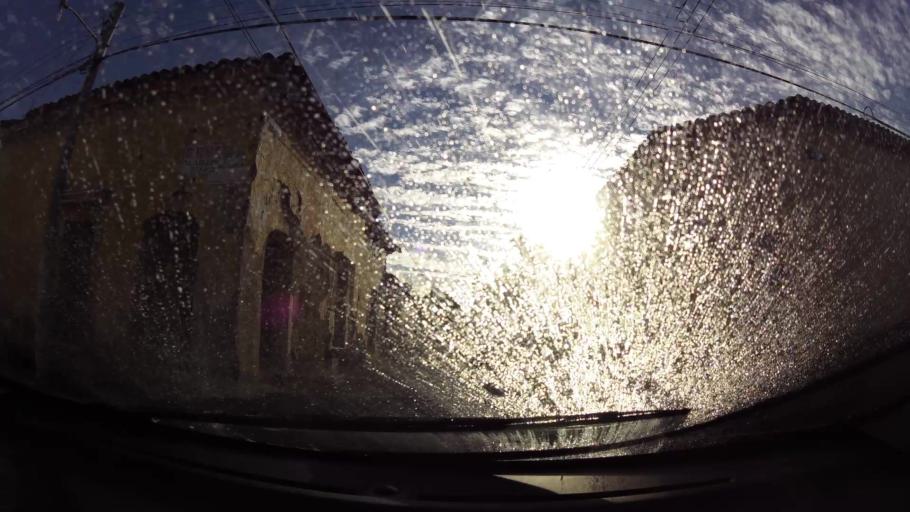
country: SV
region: Santa Ana
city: Santa Ana
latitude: 13.9936
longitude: -89.5527
